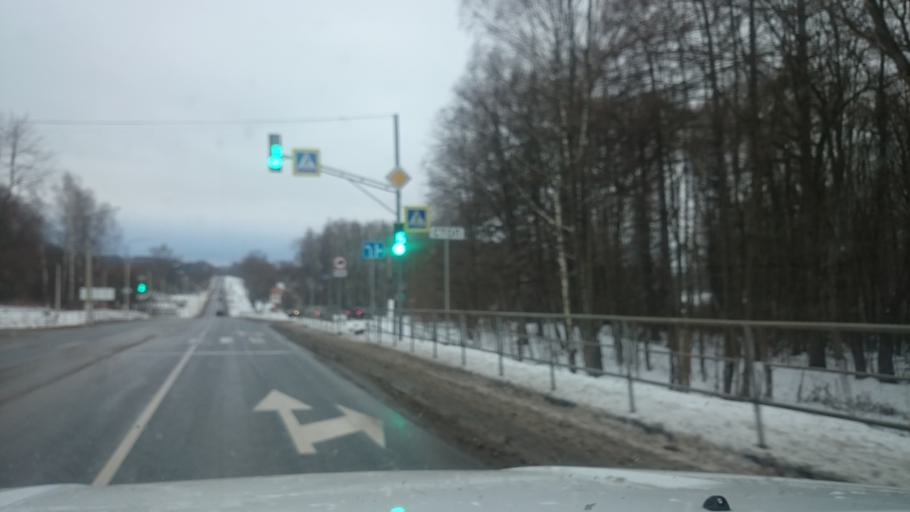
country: RU
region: Tula
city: Kosaya Gora
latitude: 54.0817
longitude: 37.5438
